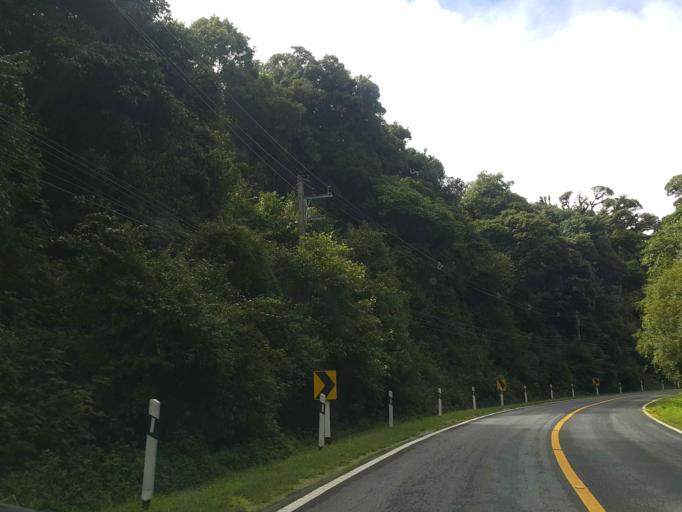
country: TH
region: Chiang Mai
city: Mae Chaem
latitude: 18.5832
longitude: 98.4799
